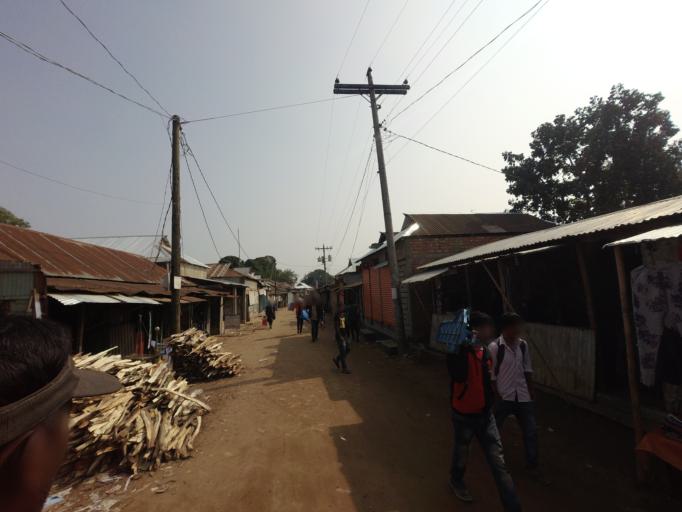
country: BD
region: Dhaka
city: Netrakona
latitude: 25.0106
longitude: 90.6479
